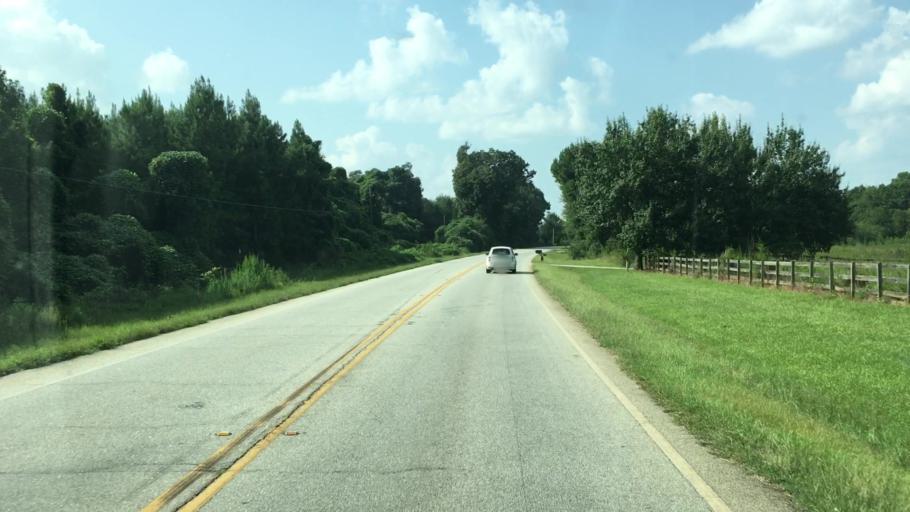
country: US
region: Georgia
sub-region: Walton County
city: Social Circle
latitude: 33.5836
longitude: -83.7467
